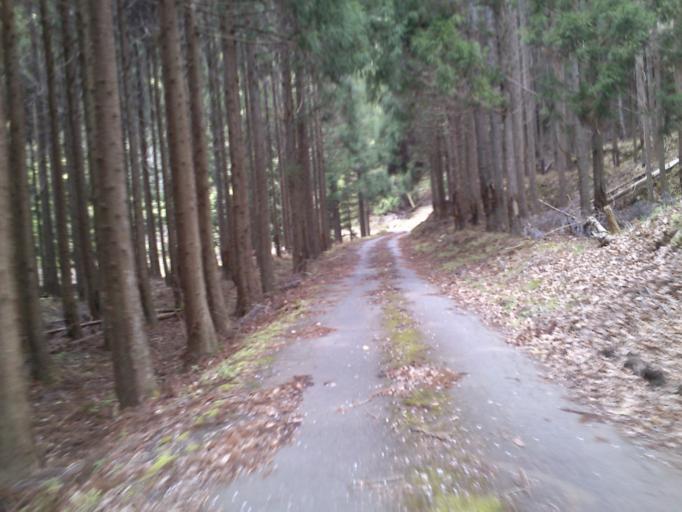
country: JP
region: Kyoto
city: Maizuru
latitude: 35.3984
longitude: 135.4946
